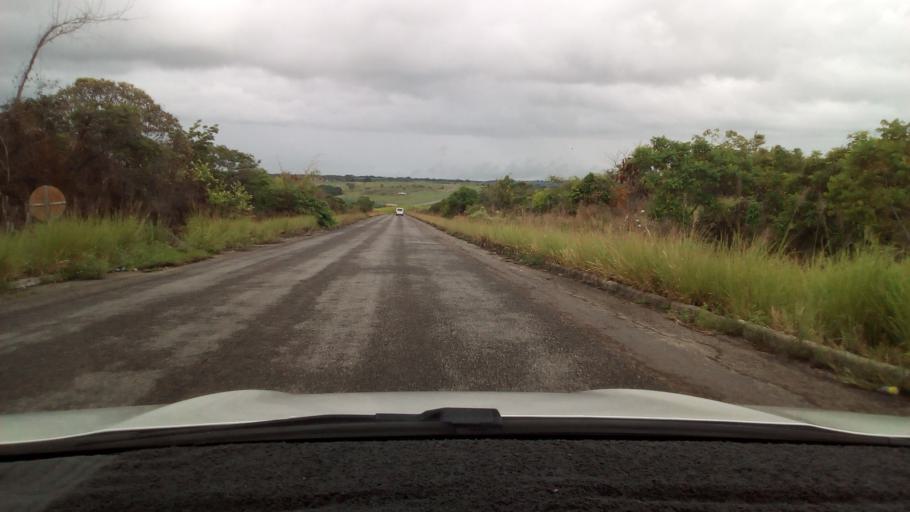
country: BR
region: Paraiba
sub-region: Pitimbu
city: Pitimbu
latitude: -7.3510
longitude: -34.8079
